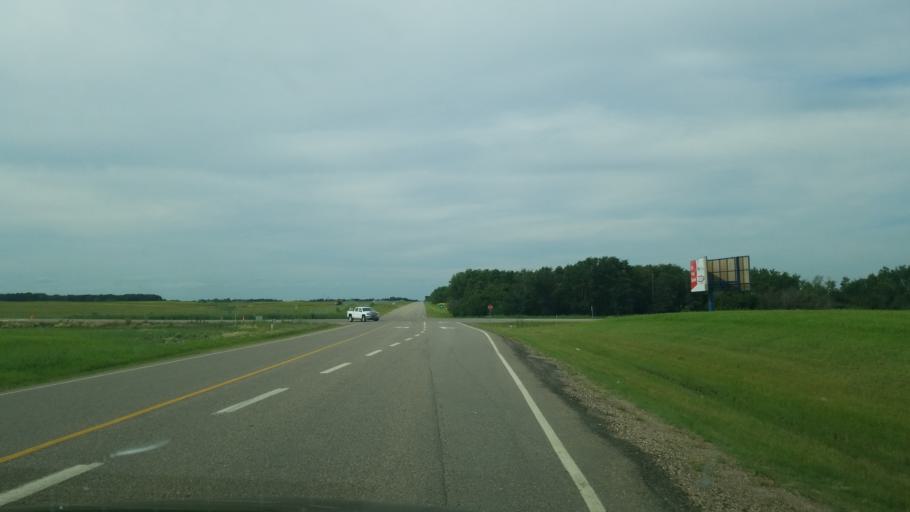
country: CA
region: Saskatchewan
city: Lloydminster
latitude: 53.3062
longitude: -110.0543
